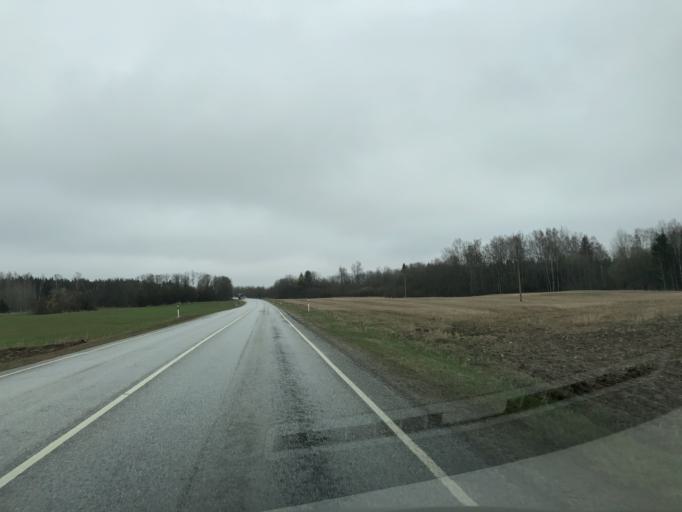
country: EE
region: Laeaene-Virumaa
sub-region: Rakke vald
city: Rakke
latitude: 58.9538
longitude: 26.2746
